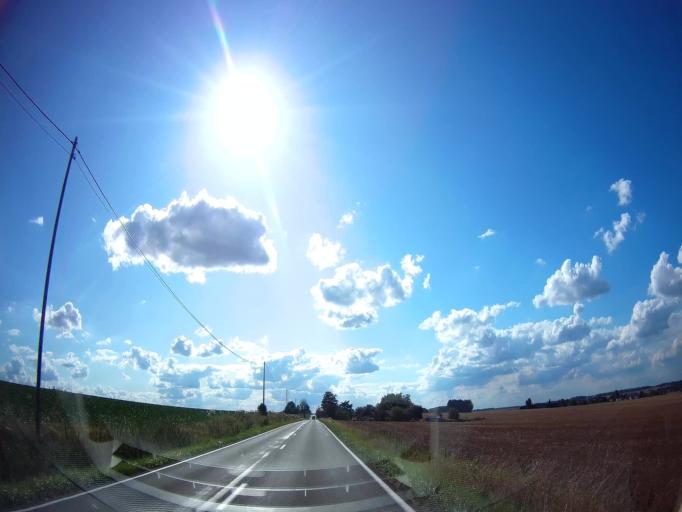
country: BE
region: Wallonia
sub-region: Province de Namur
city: Mettet
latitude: 50.3207
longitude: 4.7337
